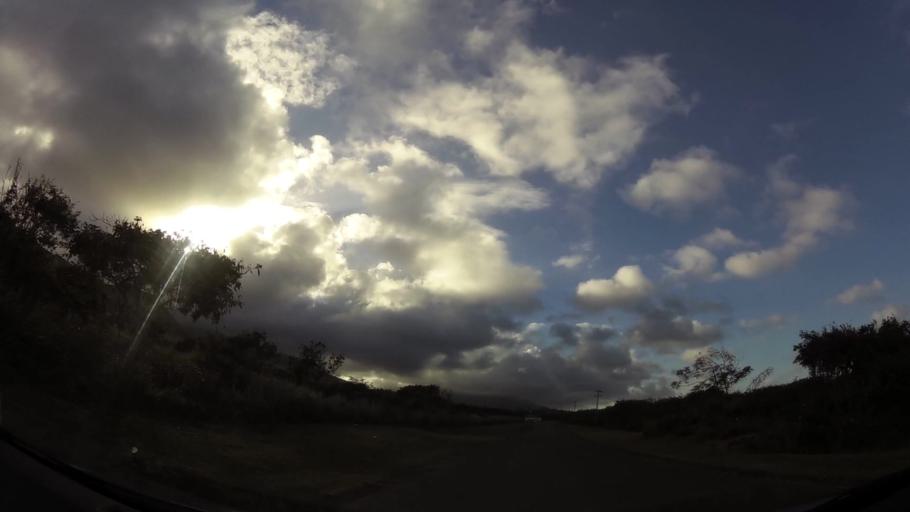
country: KN
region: Saint Mary Cayon
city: Cayon
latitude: 17.3468
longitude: -62.7222
